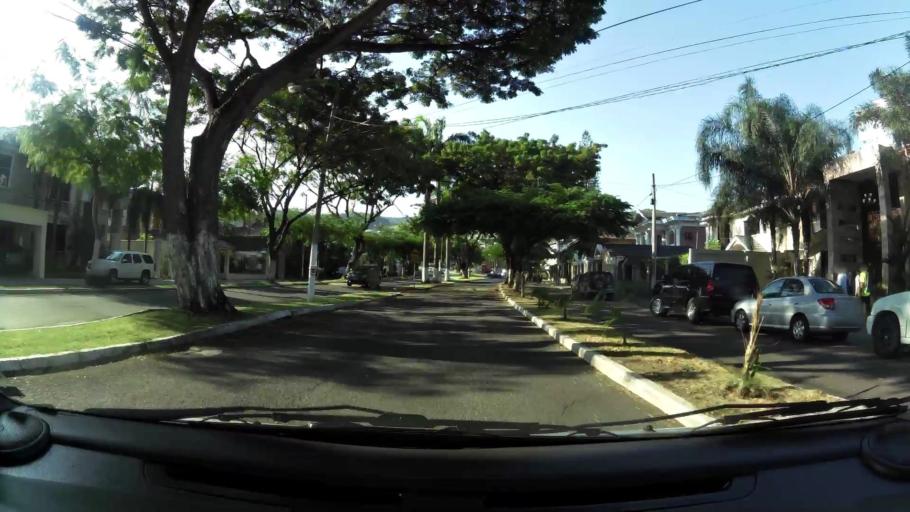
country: EC
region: Guayas
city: Santa Lucia
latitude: -2.1884
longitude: -79.9677
